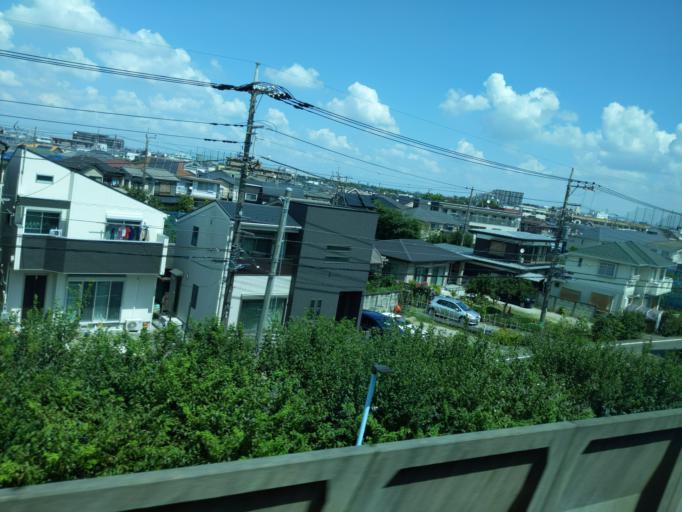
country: JP
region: Tokyo
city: Chofugaoka
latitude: 35.6429
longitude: 139.5131
